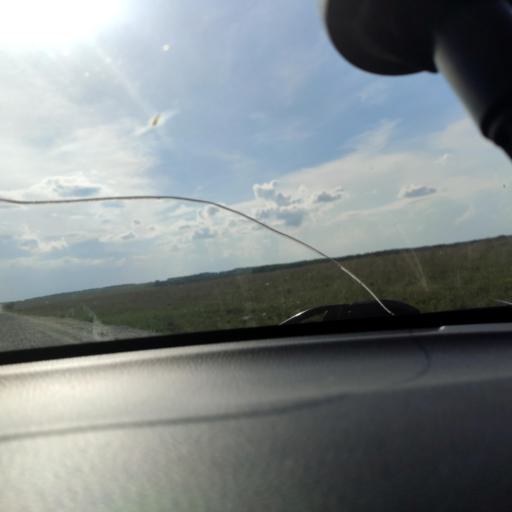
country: RU
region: Tatarstan
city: Verkhniy Uslon
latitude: 55.6465
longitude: 48.9262
